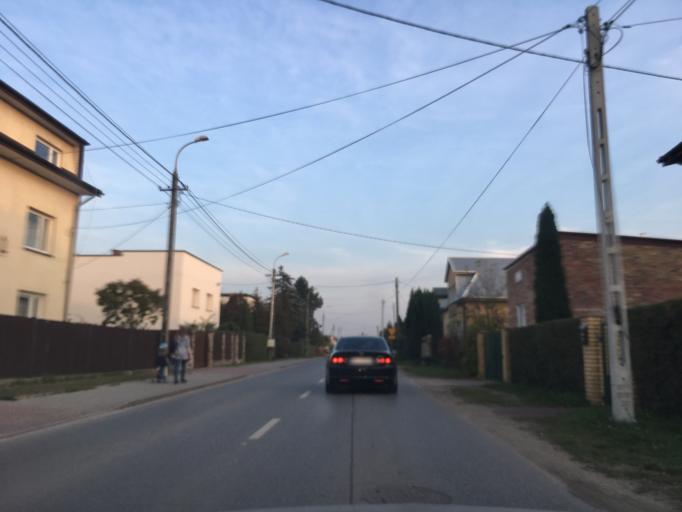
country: PL
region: Masovian Voivodeship
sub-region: Powiat piaseczynski
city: Lesznowola
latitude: 52.0828
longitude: 20.8754
